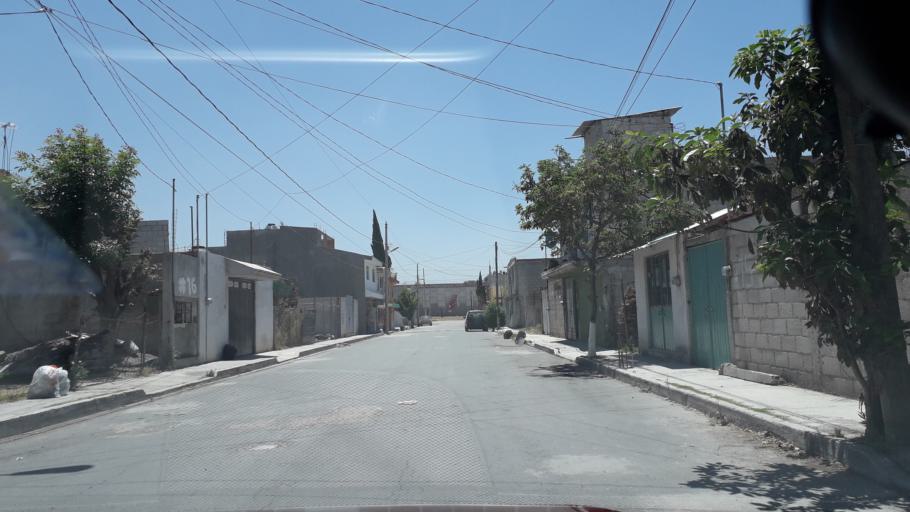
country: MX
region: Puebla
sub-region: Amozoc
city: Casa Blanca
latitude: 19.0560
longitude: -98.1166
